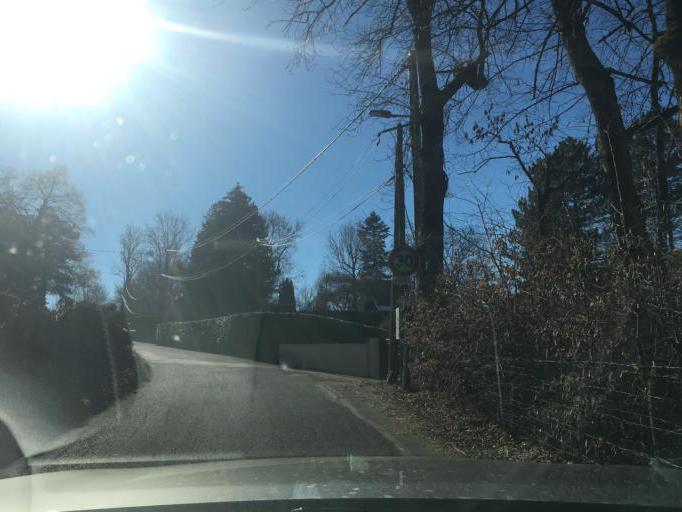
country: FR
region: Rhone-Alpes
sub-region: Departement de la Haute-Savoie
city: Vetraz-Monthoux
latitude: 46.1861
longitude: 6.2593
